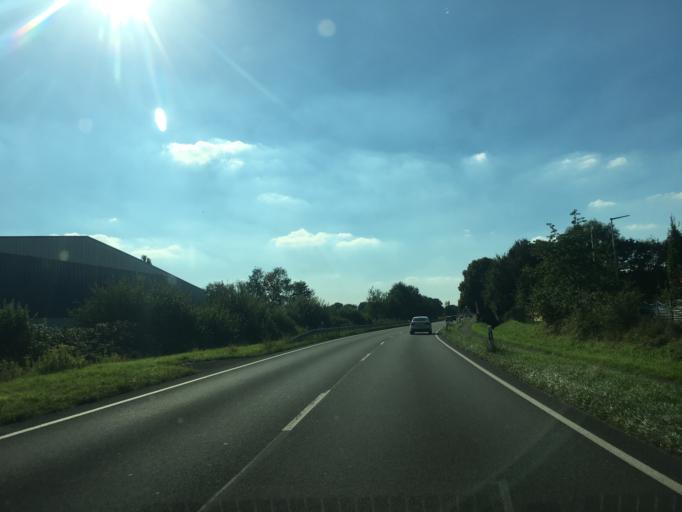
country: DE
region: North Rhine-Westphalia
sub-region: Regierungsbezirk Munster
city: Warendorf
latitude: 51.9548
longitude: 7.9677
